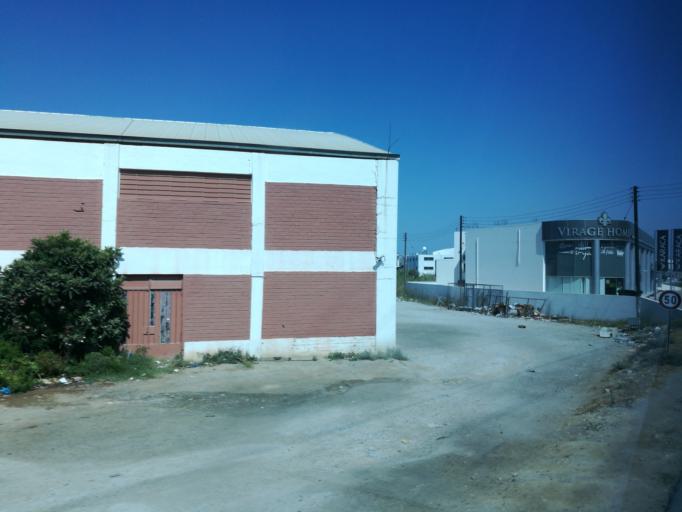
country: CY
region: Ammochostos
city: Famagusta
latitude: 35.1422
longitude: 33.9045
